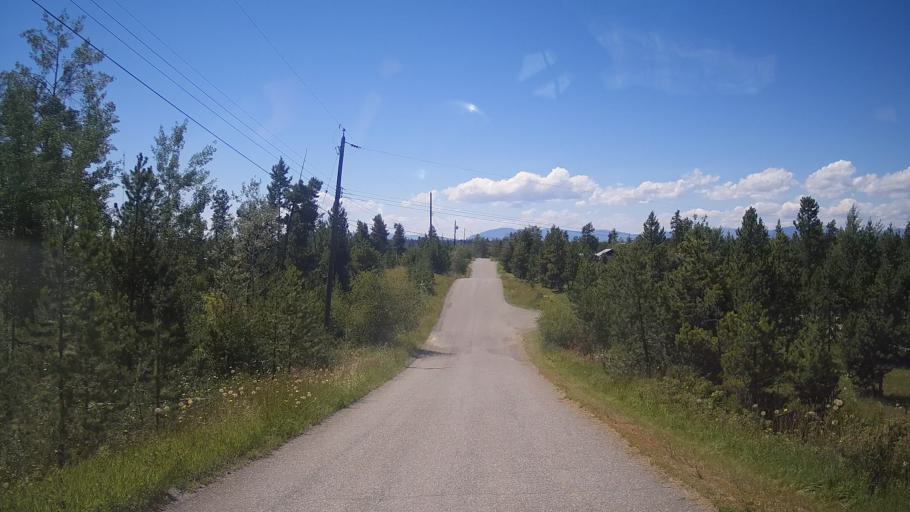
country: CA
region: British Columbia
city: Cache Creek
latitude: 51.3141
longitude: -121.3947
